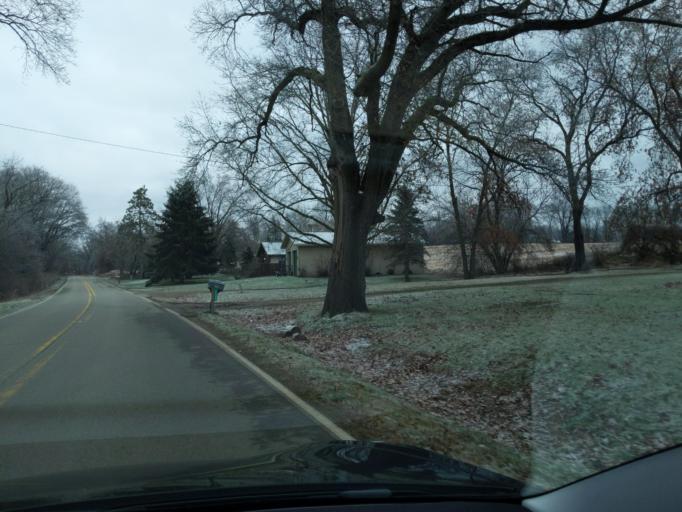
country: US
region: Michigan
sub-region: Jackson County
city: Spring Arbor
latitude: 42.1984
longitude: -84.5373
